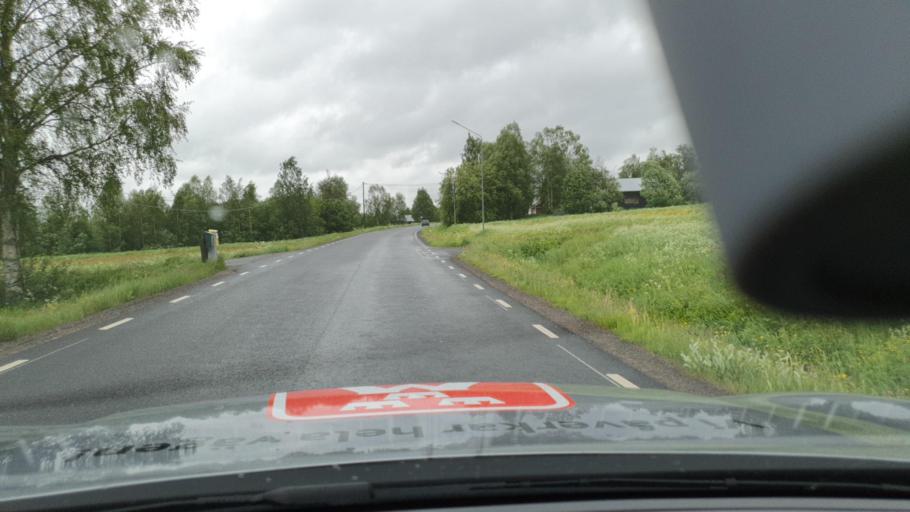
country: FI
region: Lapland
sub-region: Torniolaakso
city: Ylitornio
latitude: 66.1744
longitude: 23.8084
